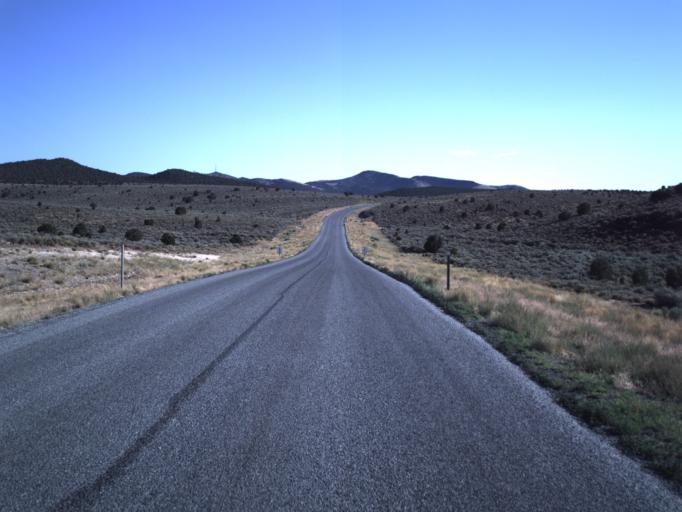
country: US
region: Utah
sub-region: Iron County
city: Parowan
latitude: 38.0295
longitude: -112.9982
